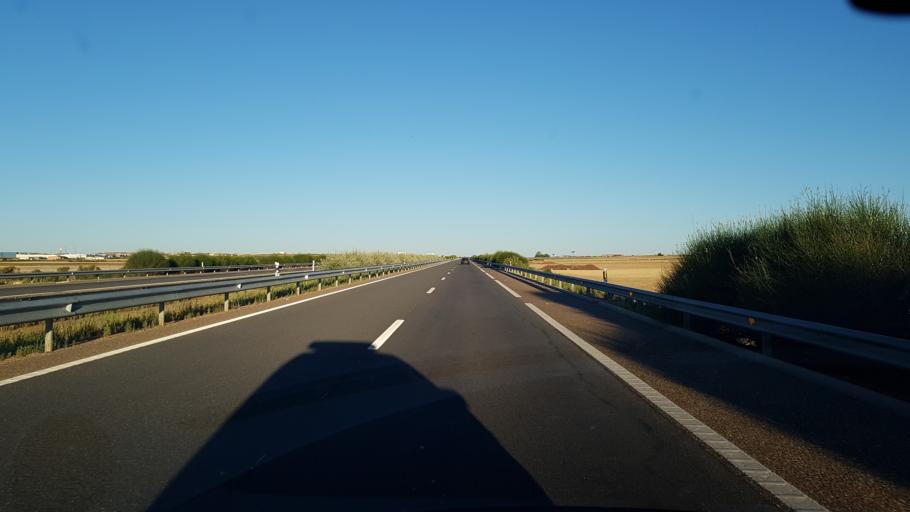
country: ES
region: Castille and Leon
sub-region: Provincia de Zamora
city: Villavendimio
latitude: 41.5409
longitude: -5.3491
